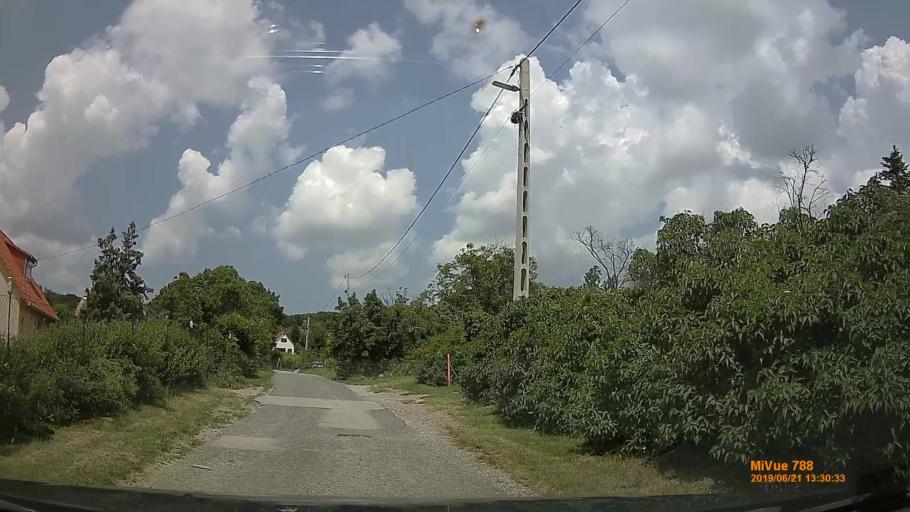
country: HU
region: Baranya
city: Pellerd
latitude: 46.0627
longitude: 18.1361
